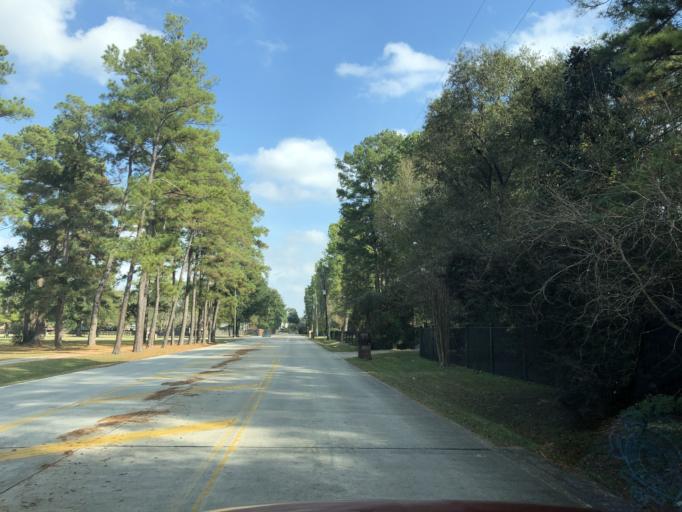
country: US
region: Texas
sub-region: Harris County
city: Tomball
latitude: 30.0272
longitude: -95.5484
